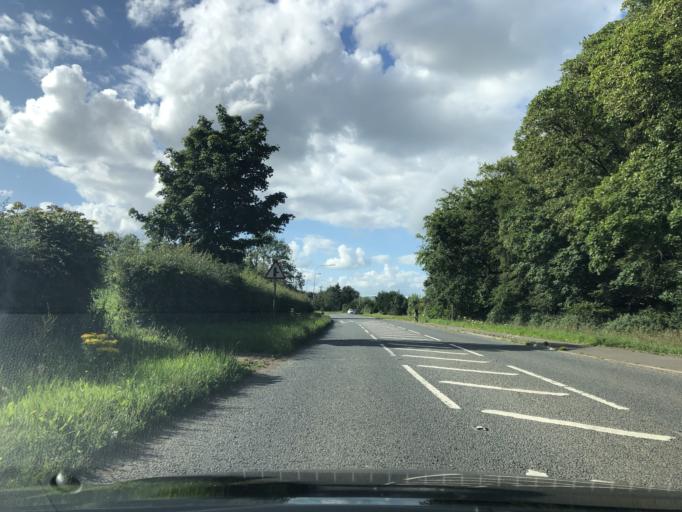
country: GB
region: Northern Ireland
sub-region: Ards District
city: Comber
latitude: 54.5667
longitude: -5.7679
